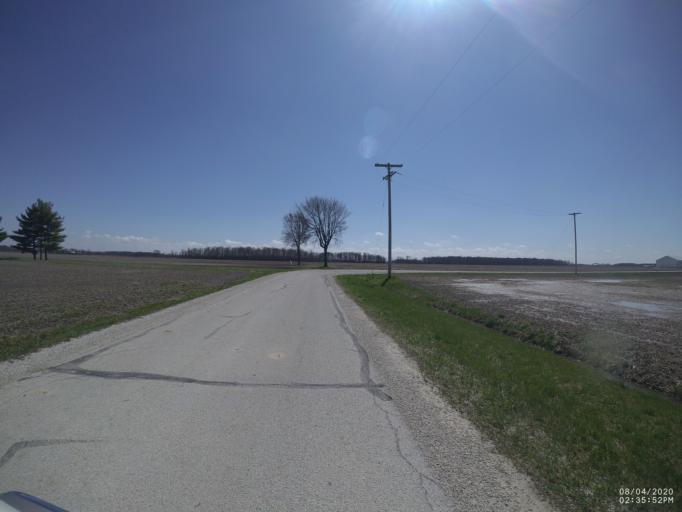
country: US
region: Ohio
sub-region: Sandusky County
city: Gibsonburg
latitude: 41.2799
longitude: -83.2928
